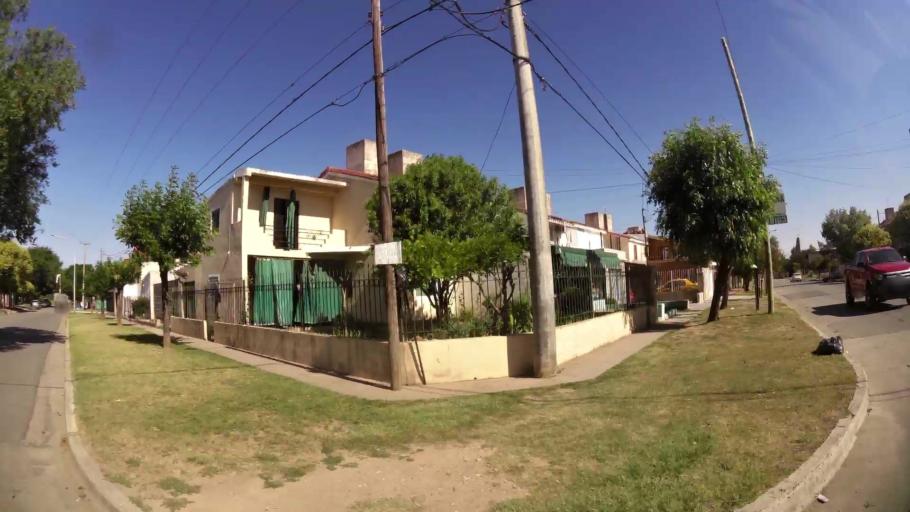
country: AR
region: Cordoba
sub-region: Departamento de Capital
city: Cordoba
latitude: -31.3578
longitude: -64.1833
